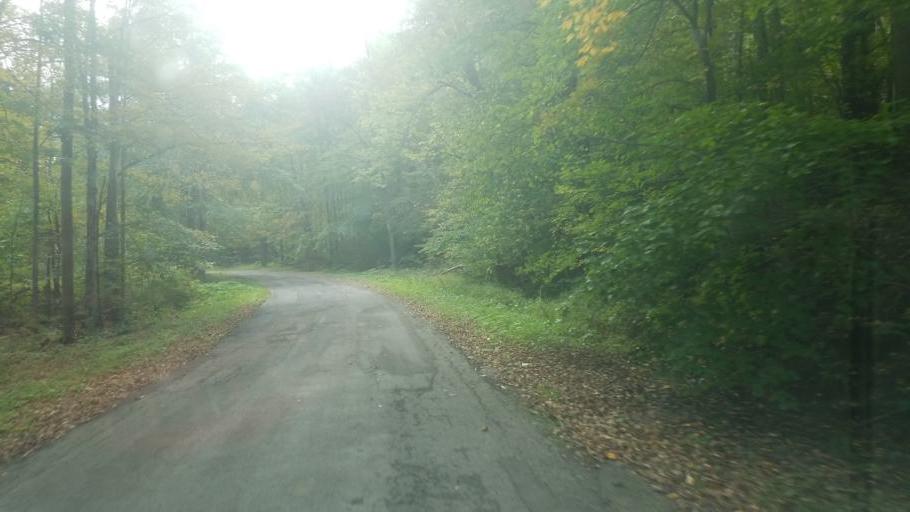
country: US
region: New York
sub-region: Allegany County
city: Cuba
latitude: 42.2219
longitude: -78.3420
